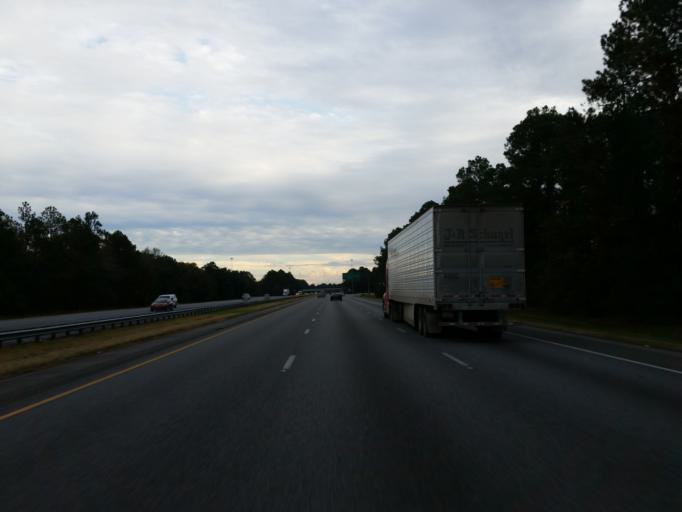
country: US
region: Georgia
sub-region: Lowndes County
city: Valdosta
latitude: 30.7862
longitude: -83.2999
